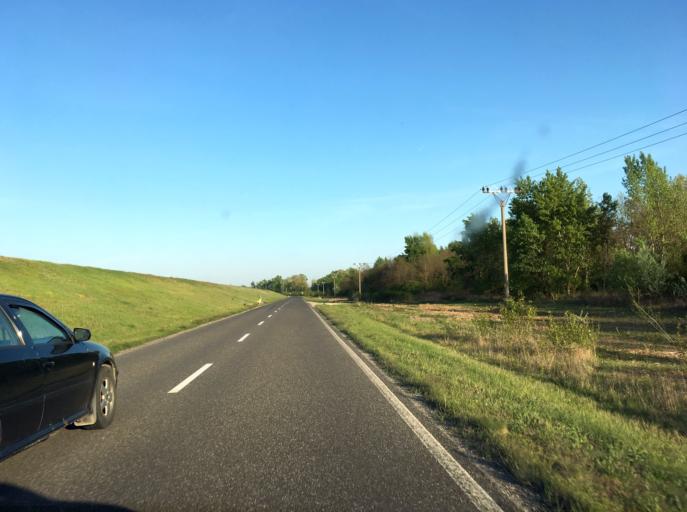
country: SK
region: Trnavsky
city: Samorin
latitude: 47.9995
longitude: 17.2649
